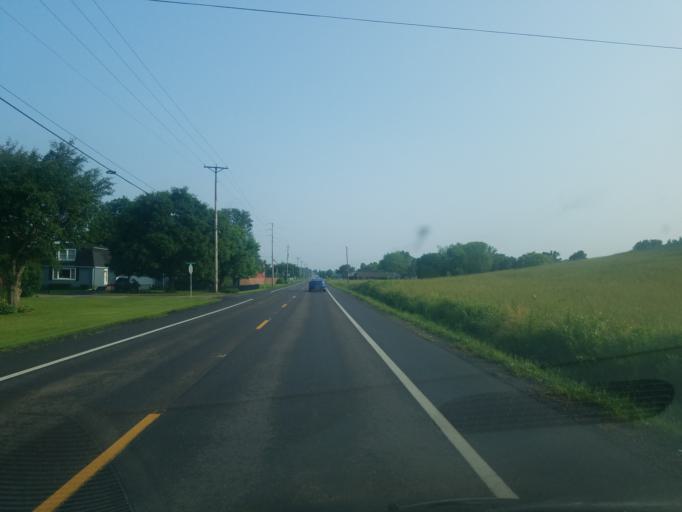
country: US
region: Ohio
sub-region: Tuscarawas County
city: Strasburg
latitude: 40.6250
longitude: -81.4347
